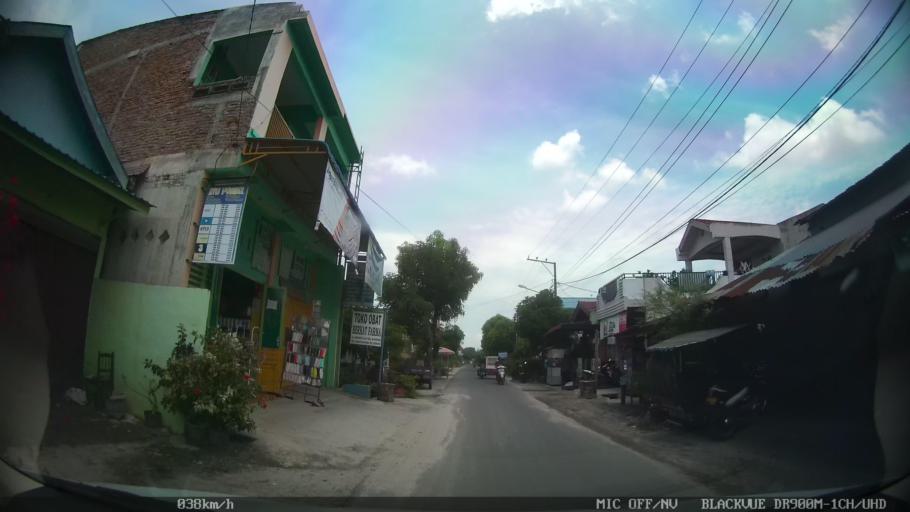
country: ID
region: North Sumatra
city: Percut
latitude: 3.5495
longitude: 98.8723
